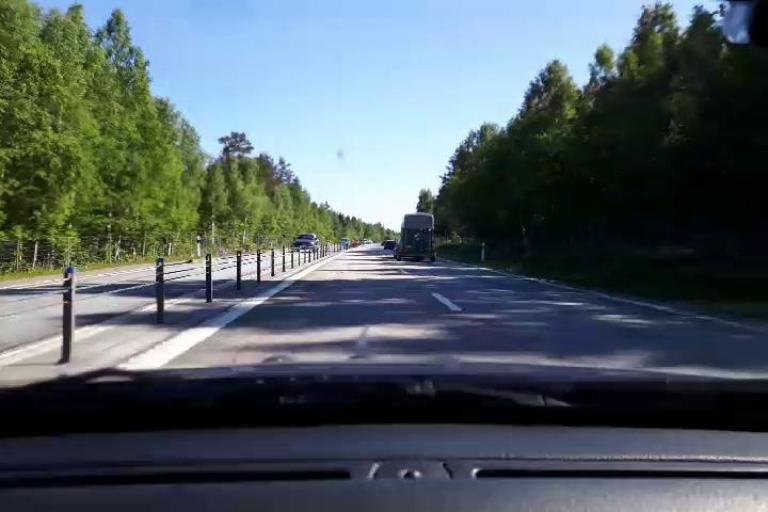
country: SE
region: Gaevleborg
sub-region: Gavle Kommun
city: Norrsundet
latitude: 60.9228
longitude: 17.0113
